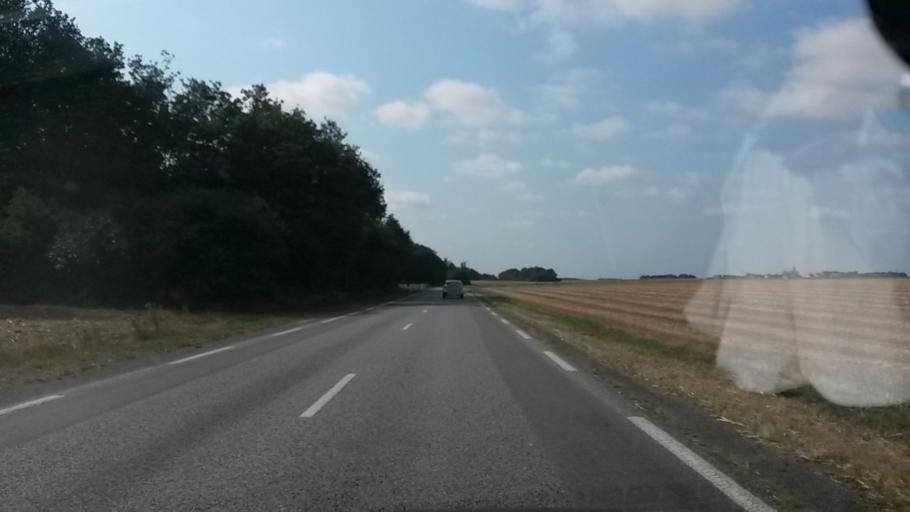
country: FR
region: Haute-Normandie
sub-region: Departement de l'Eure
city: Tillieres-sur-Avre
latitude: 48.8171
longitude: 1.0058
